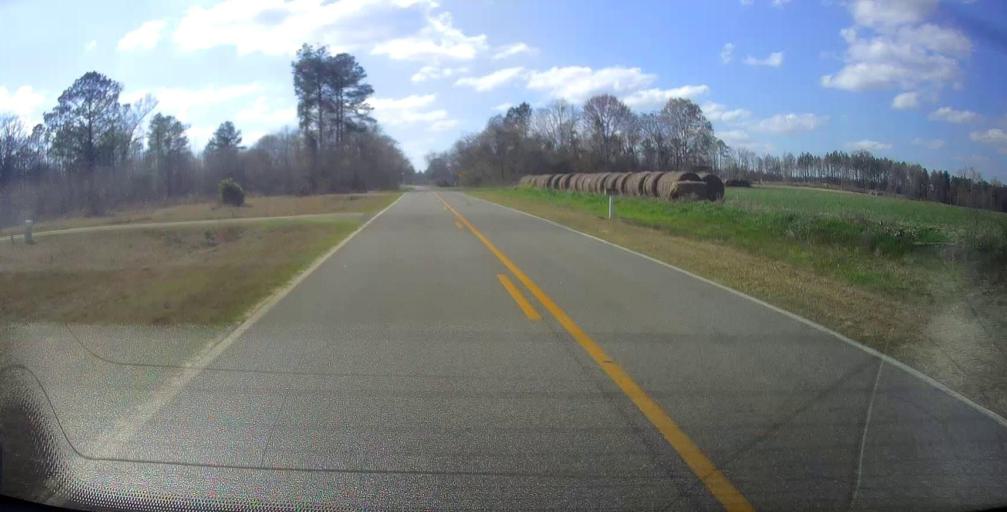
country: US
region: Georgia
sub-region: Wilkinson County
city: Irwinton
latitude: 32.6336
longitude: -83.1119
